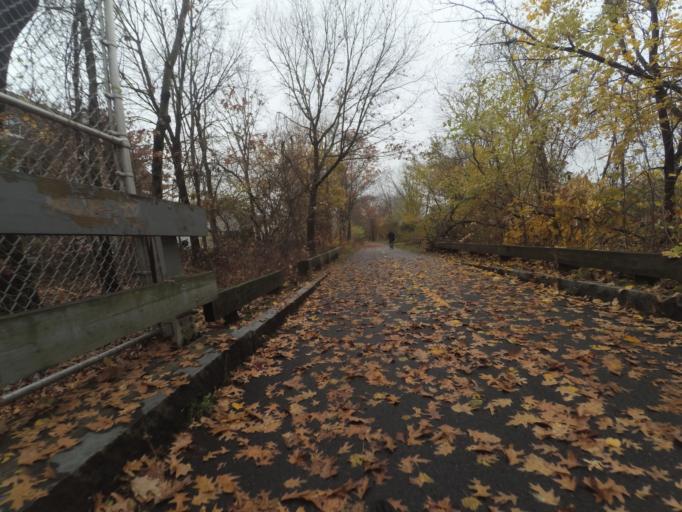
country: US
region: Massachusetts
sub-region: Middlesex County
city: Belmont
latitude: 42.4254
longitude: -71.1861
